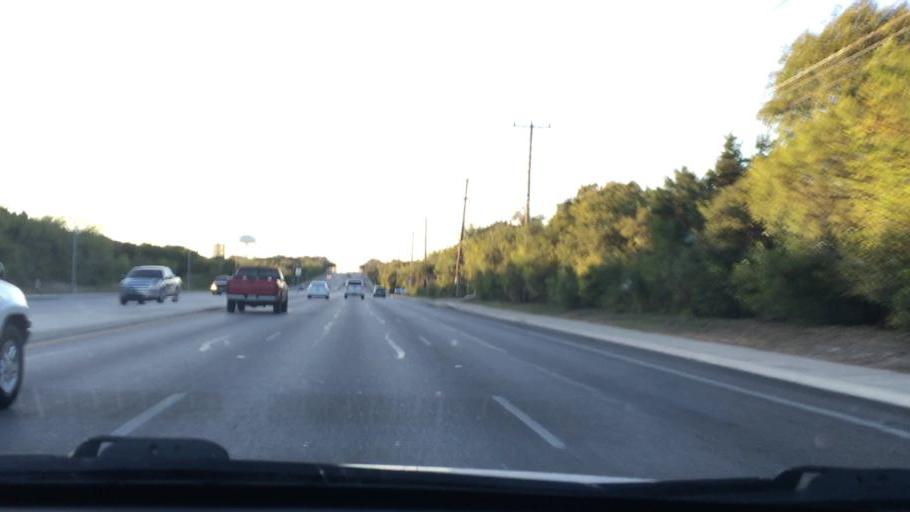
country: US
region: Texas
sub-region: Bexar County
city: Castle Hills
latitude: 29.5533
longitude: -98.5332
